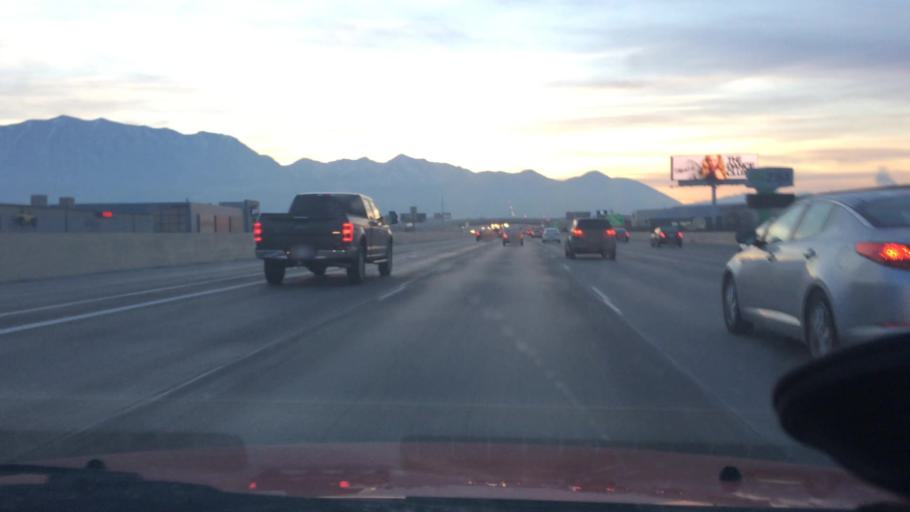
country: US
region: Utah
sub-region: Utah County
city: Lindon
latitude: 40.3370
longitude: -111.7490
